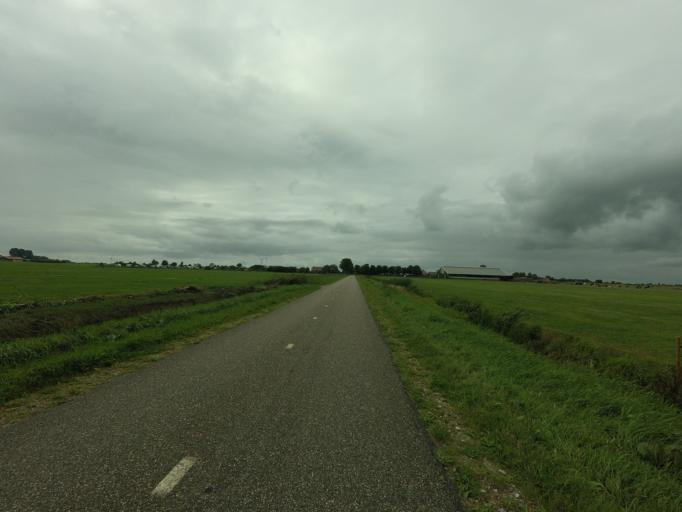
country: NL
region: Friesland
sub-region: Sudwest Fryslan
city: Workum
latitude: 52.9762
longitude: 5.5025
